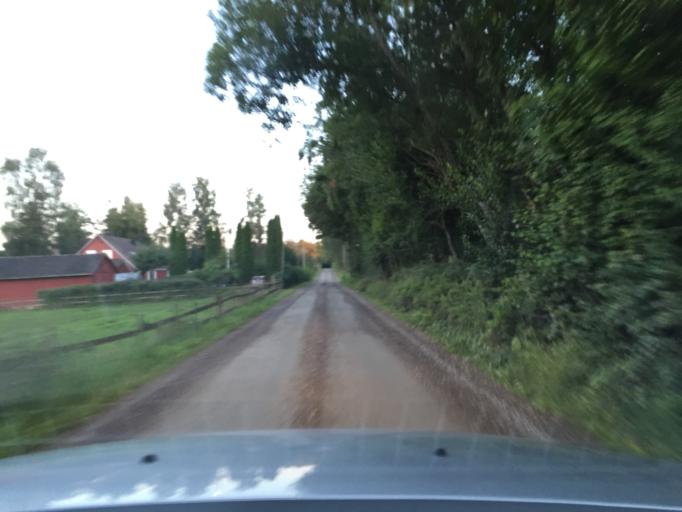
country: SE
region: Skane
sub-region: Hassleholms Kommun
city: Sosdala
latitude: 56.0050
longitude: 13.6601
